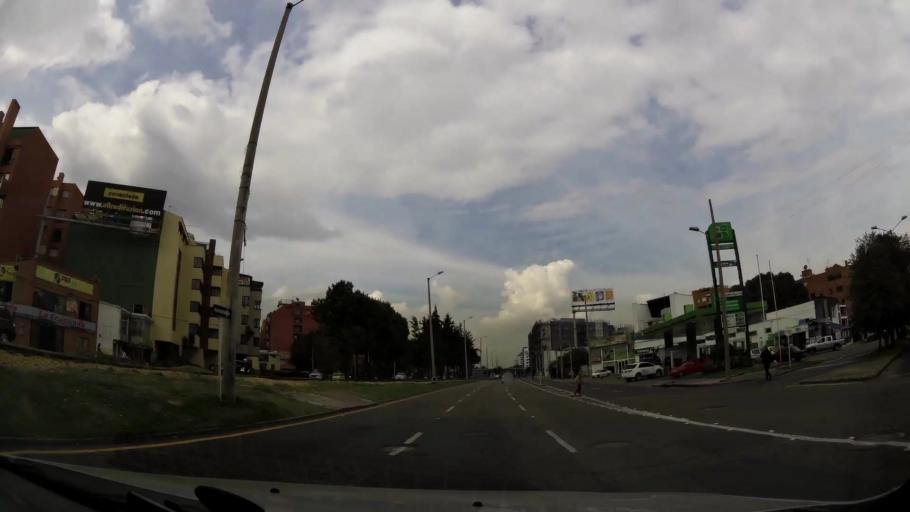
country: CO
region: Bogota D.C.
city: Barrio San Luis
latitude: 4.6874
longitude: -74.0441
